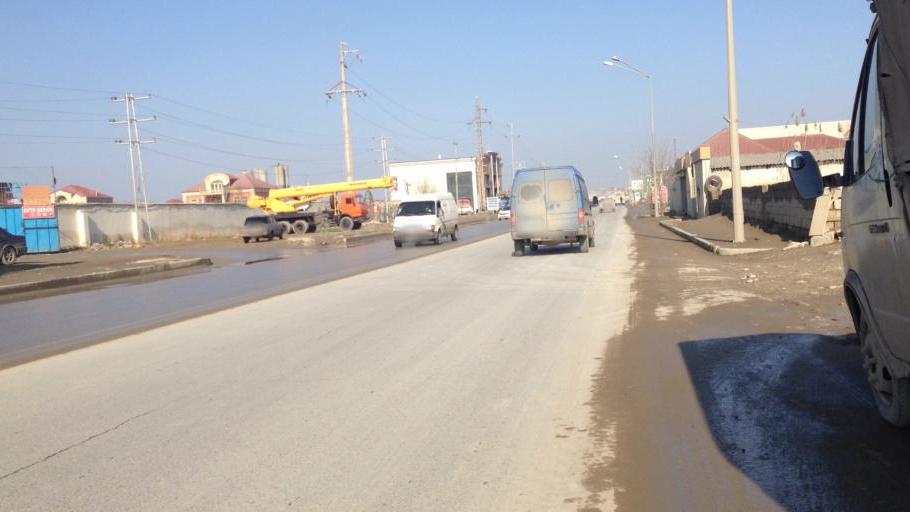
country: AZ
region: Baki
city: Binagadi
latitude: 40.4462
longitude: 49.8441
